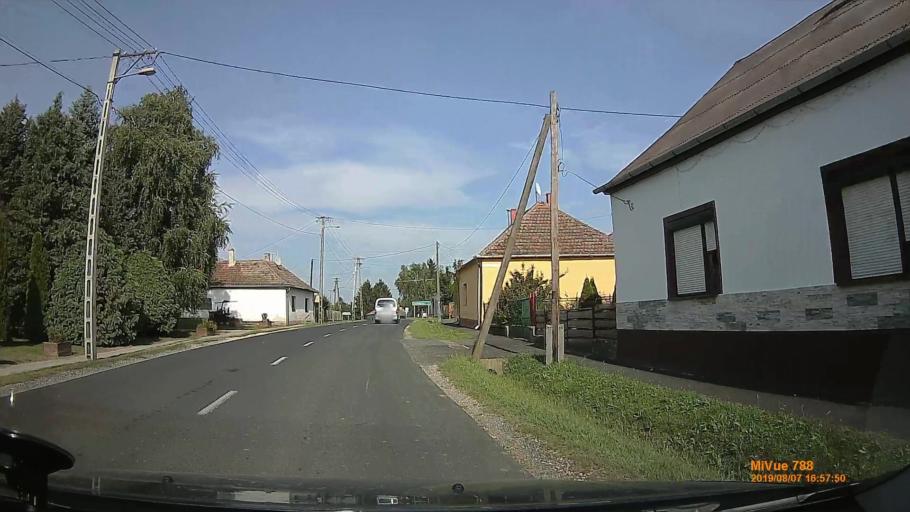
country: HU
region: Zala
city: Zalaegerszeg
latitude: 46.7010
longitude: 16.7582
